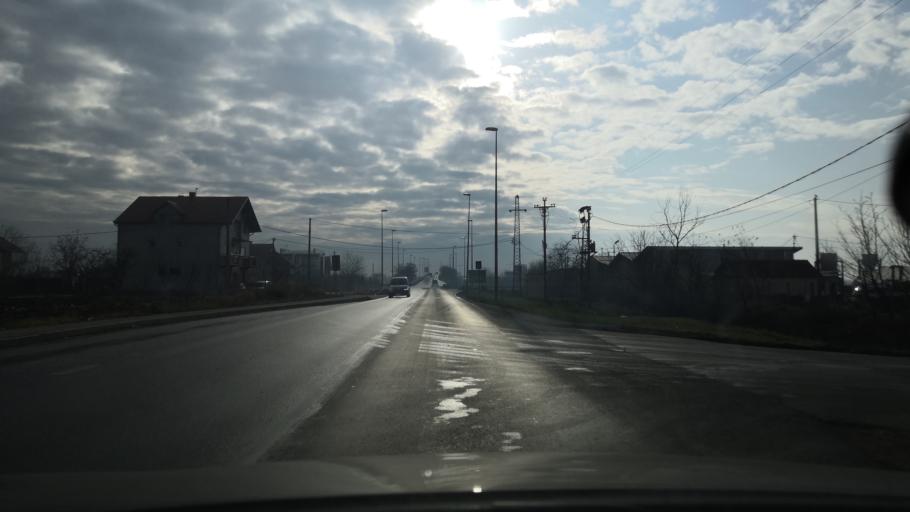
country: RS
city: Dobanovci
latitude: 44.8486
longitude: 20.2086
